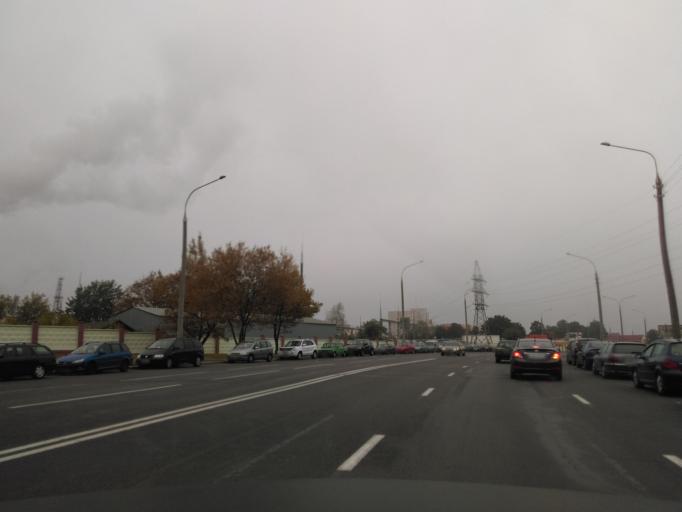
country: BY
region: Minsk
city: Minsk
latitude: 53.8827
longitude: 27.5798
